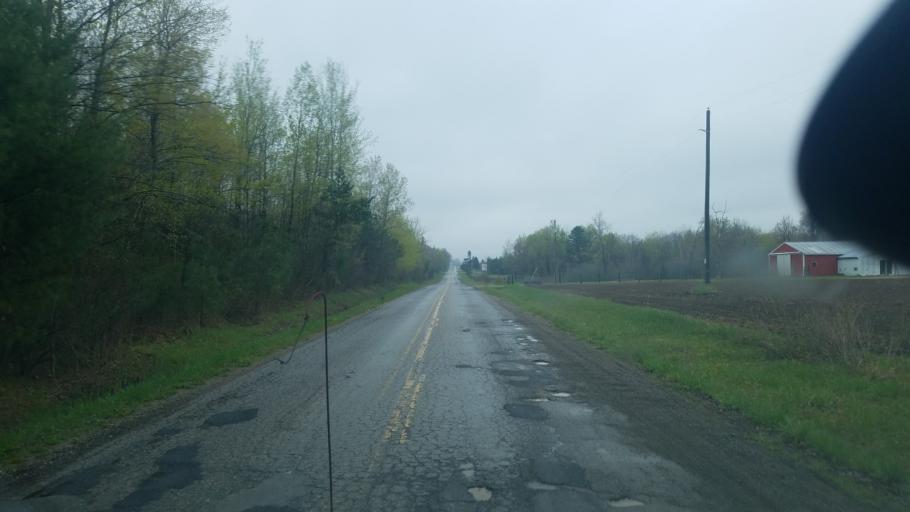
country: US
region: Michigan
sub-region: Mecosta County
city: Canadian Lakes
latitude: 43.5720
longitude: -85.3936
